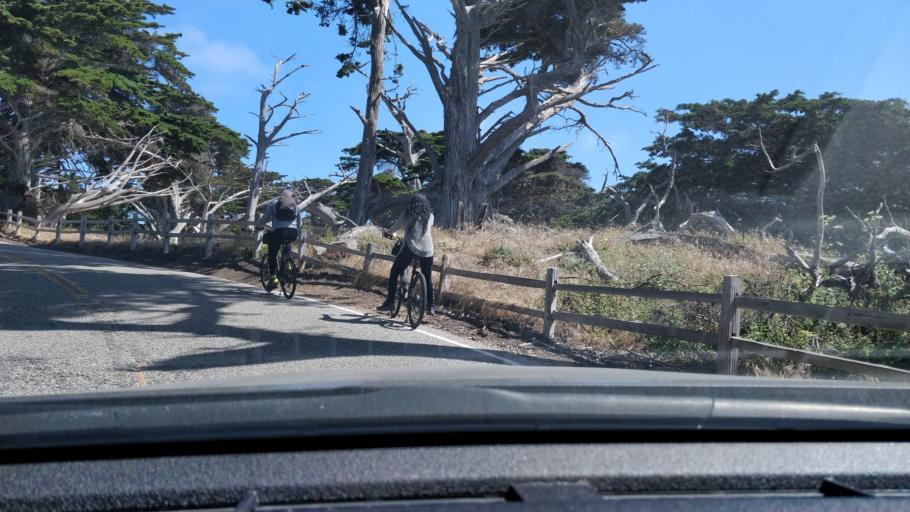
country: US
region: California
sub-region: Monterey County
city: Del Monte Forest
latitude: 36.5822
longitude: -121.9738
